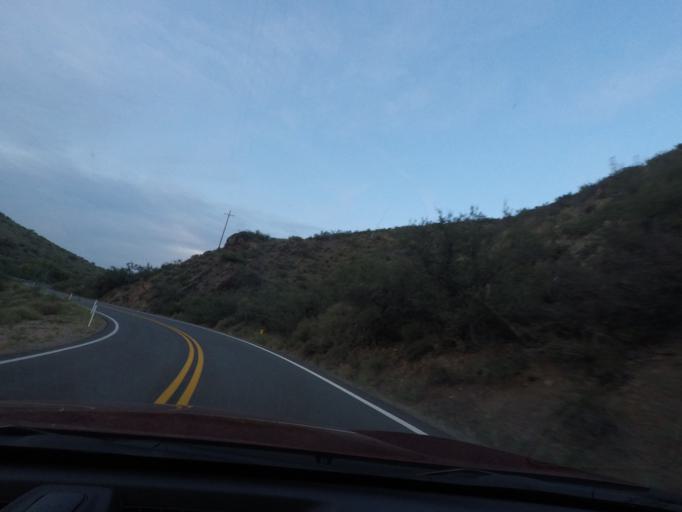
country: US
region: Arizona
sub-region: Yavapai County
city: Prescott
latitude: 34.4230
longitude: -112.6995
